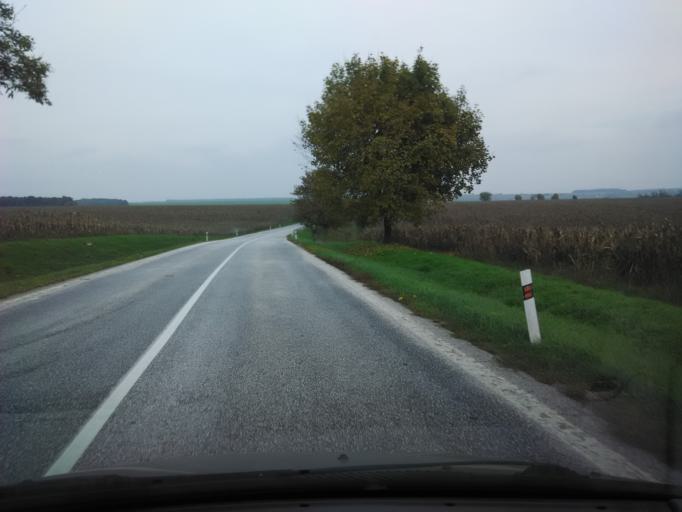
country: SK
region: Nitriansky
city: Svodin
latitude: 48.0093
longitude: 18.3788
